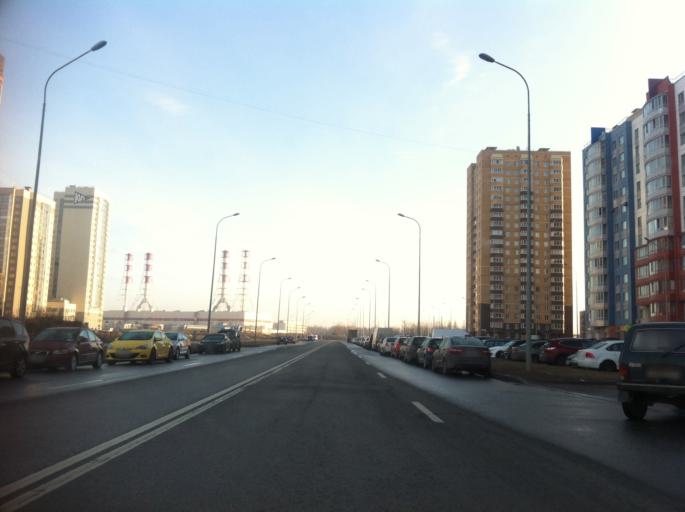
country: RU
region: St.-Petersburg
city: Uritsk
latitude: 59.8622
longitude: 30.1804
